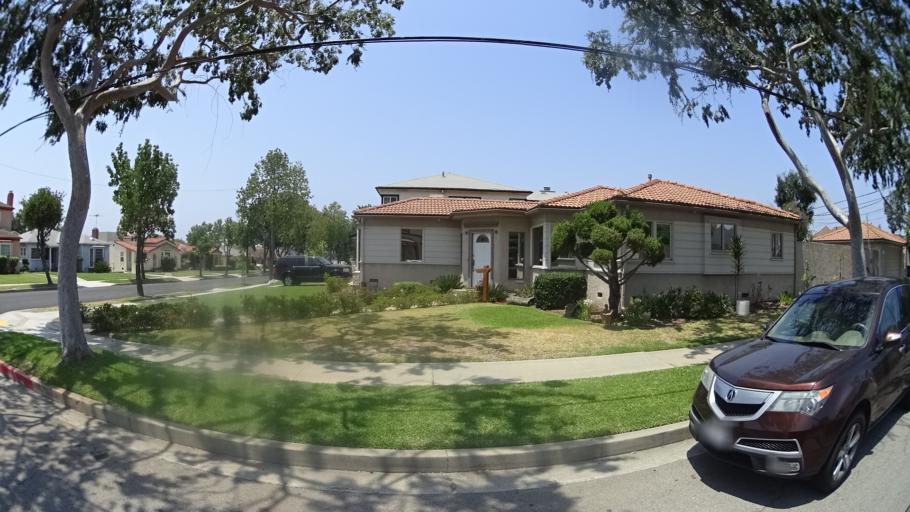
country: US
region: California
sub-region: Los Angeles County
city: Inglewood
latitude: 33.9629
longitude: -118.3332
